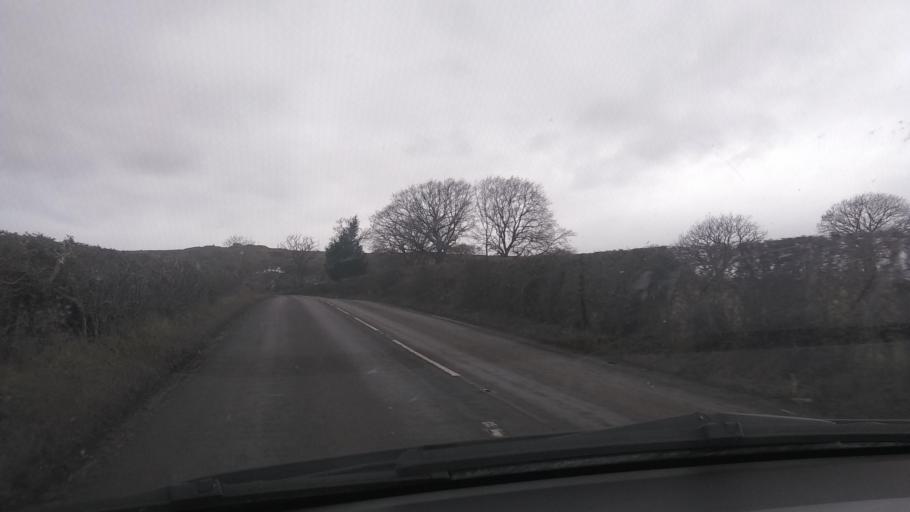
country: GB
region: England
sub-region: Shropshire
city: Cleobury Mortimer
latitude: 52.3868
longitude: -2.5505
